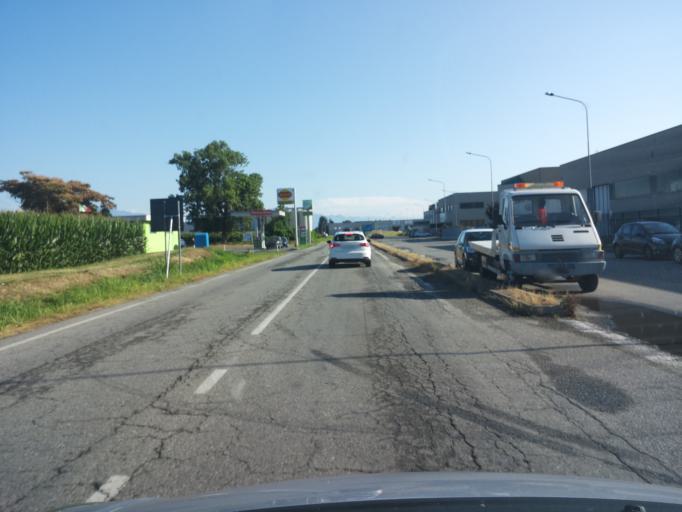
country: IT
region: Piedmont
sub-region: Provincia di Vercelli
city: Santhia
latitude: 45.3735
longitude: 8.1509
